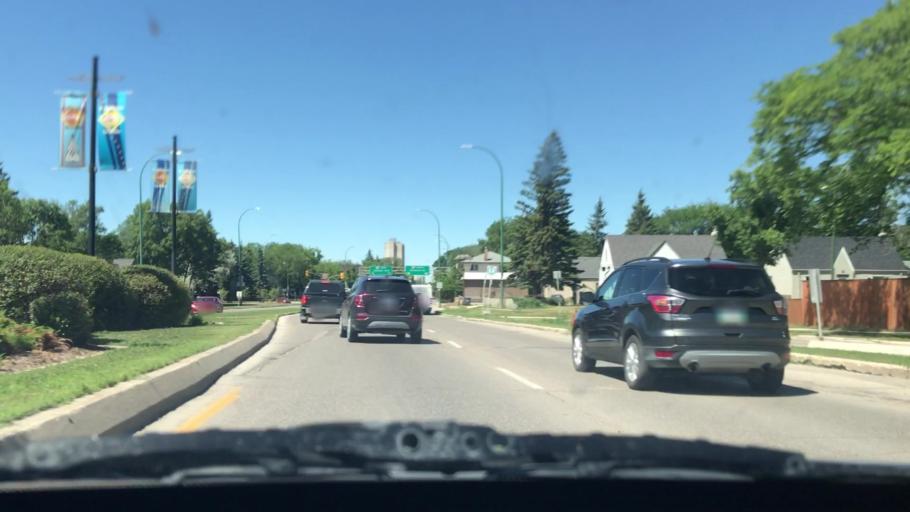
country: CA
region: Manitoba
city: Winnipeg
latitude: 49.8582
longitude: -97.1286
